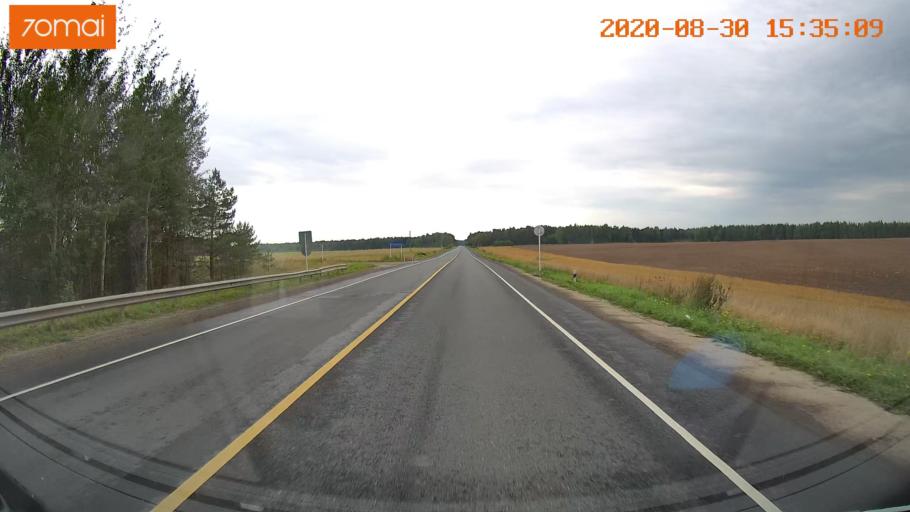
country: RU
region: Ivanovo
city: Kaminskiy
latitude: 57.0655
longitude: 41.4111
